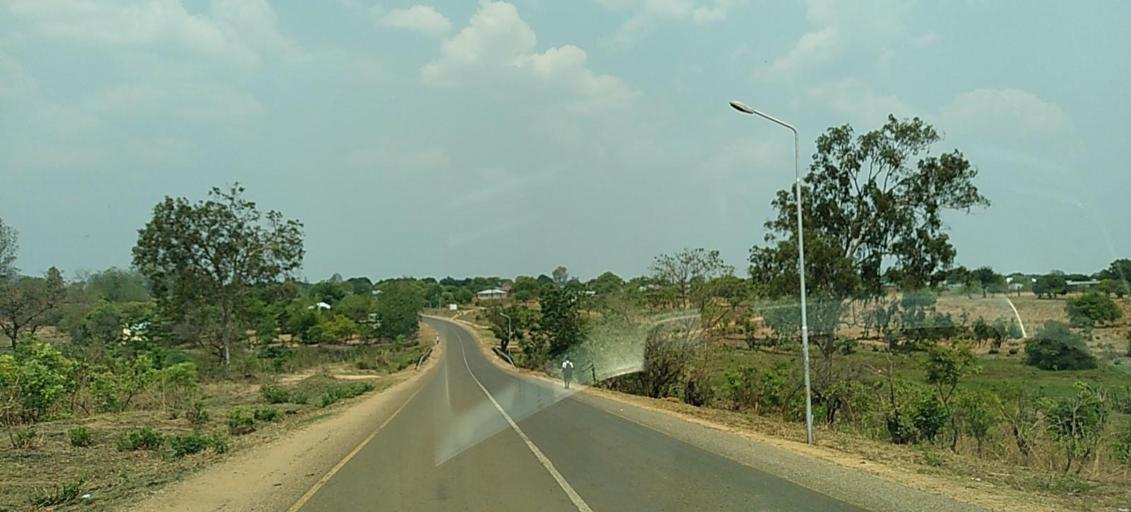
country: ZM
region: North-Western
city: Zambezi
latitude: -13.5497
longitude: 23.1069
